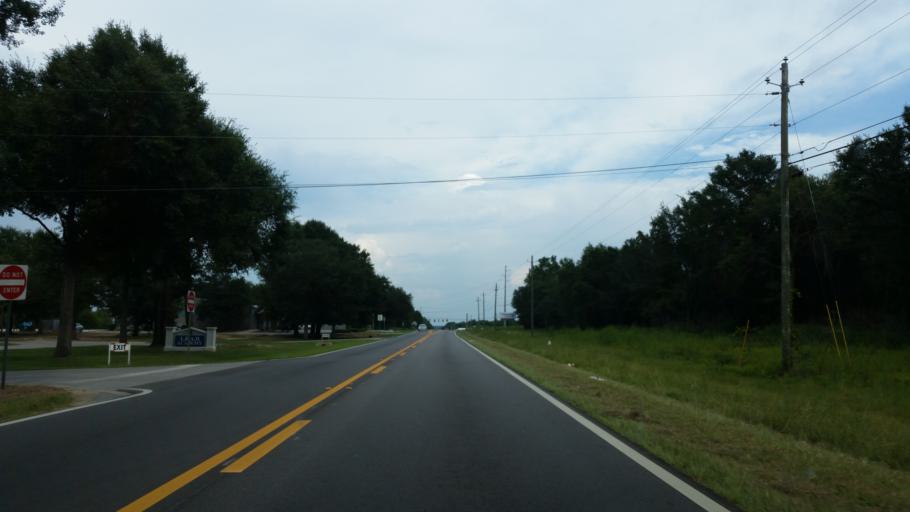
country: US
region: Florida
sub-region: Santa Rosa County
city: Wallace
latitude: 30.6474
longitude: -87.1517
